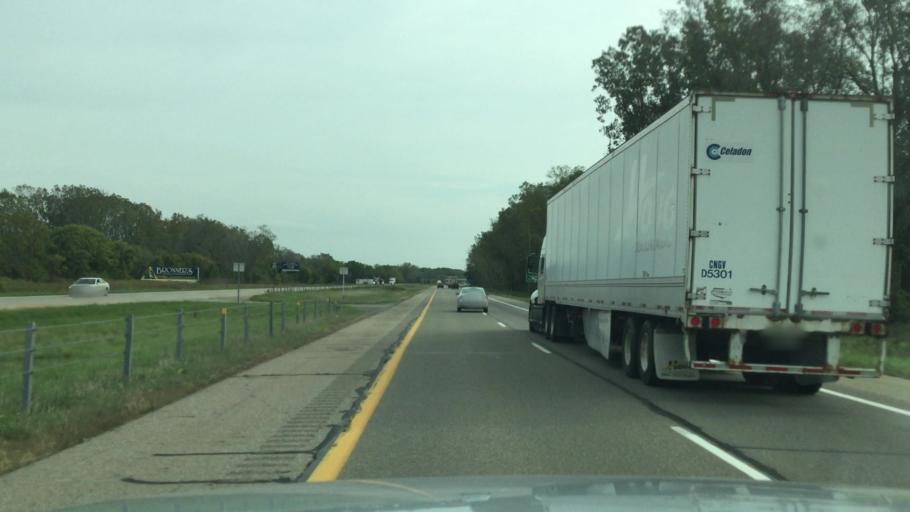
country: US
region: Michigan
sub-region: Shiawassee County
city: Durand
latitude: 42.9633
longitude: -83.9442
